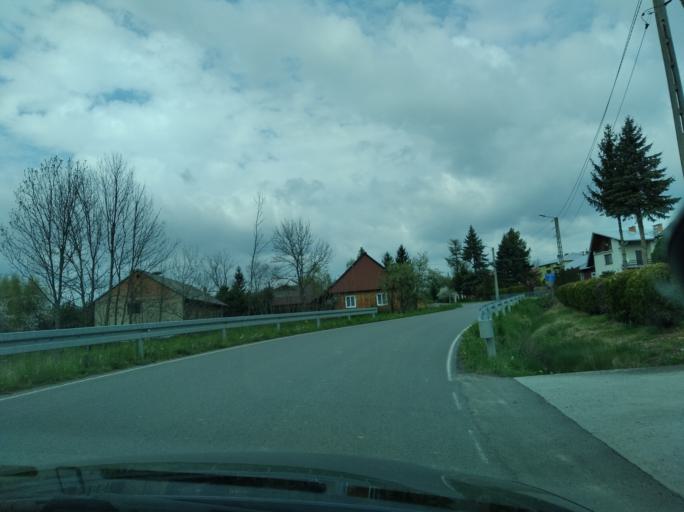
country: PL
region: Subcarpathian Voivodeship
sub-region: Powiat brzozowski
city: Haczow
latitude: 49.6548
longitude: 21.9100
